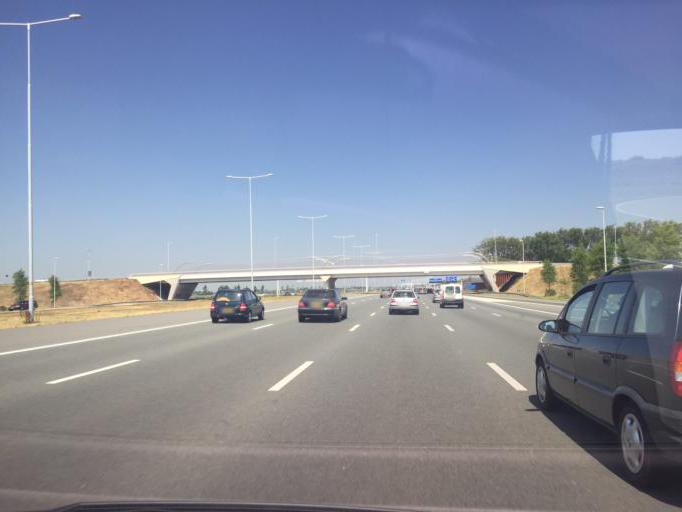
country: NL
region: North Holland
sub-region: Gemeente Amsterdam
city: Amsterdam-Zuidoost
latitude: 52.2649
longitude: 4.9629
